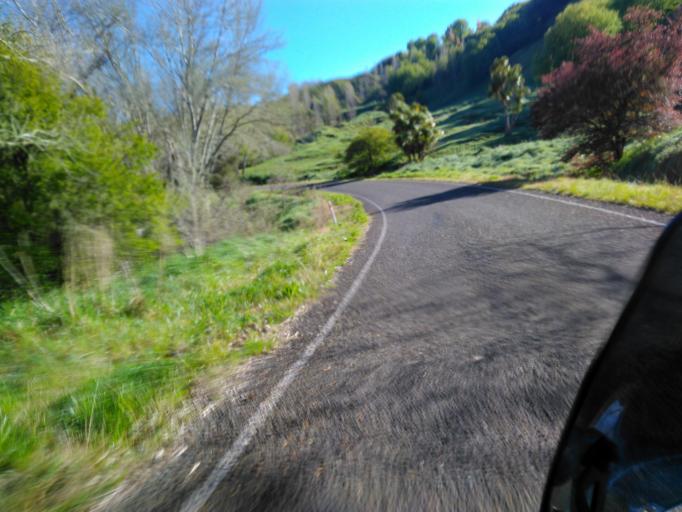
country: NZ
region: Gisborne
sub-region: Gisborne District
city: Gisborne
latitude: -38.4449
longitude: 177.7617
